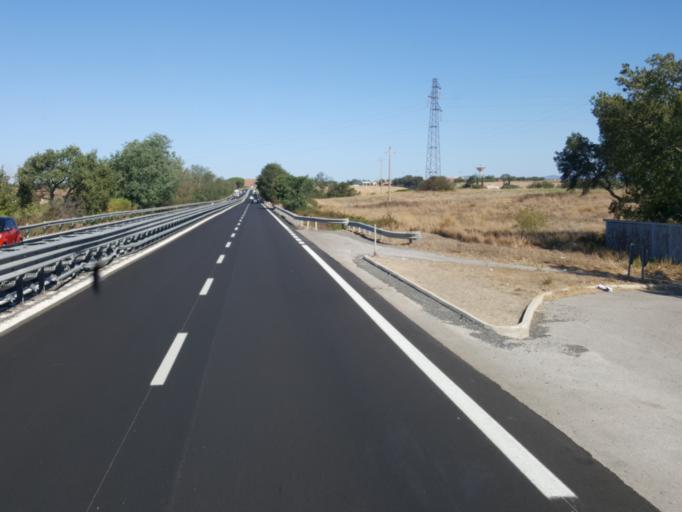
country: IT
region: Latium
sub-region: Provincia di Viterbo
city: Montalto di Castro
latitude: 42.3332
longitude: 11.6260
